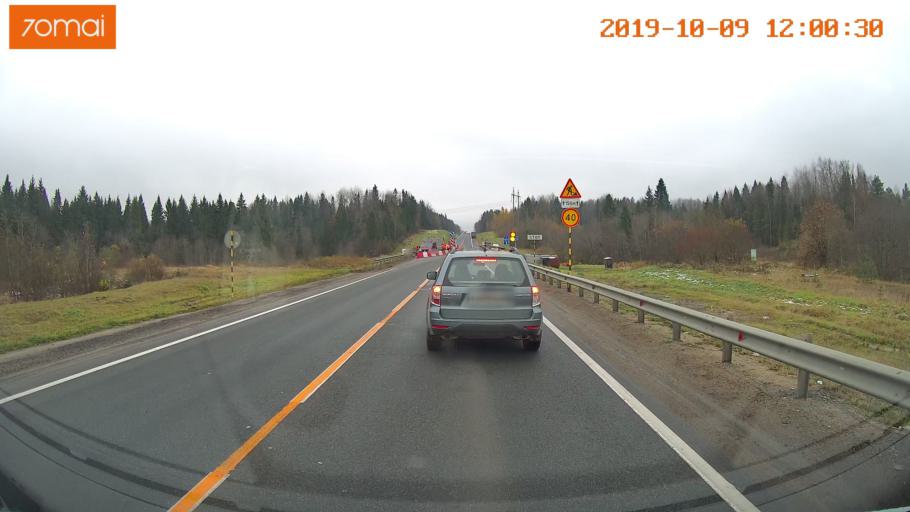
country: RU
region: Vologda
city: Gryazovets
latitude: 58.6957
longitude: 40.3001
